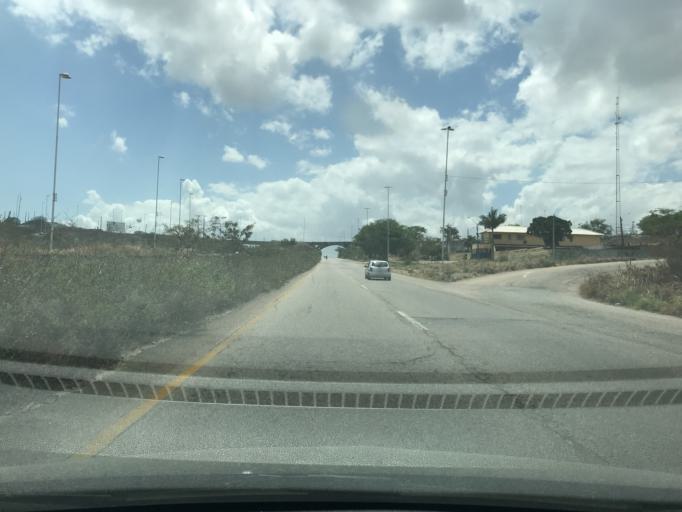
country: BR
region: Pernambuco
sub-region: Caruaru
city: Caruaru
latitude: -8.3068
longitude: -35.9617
